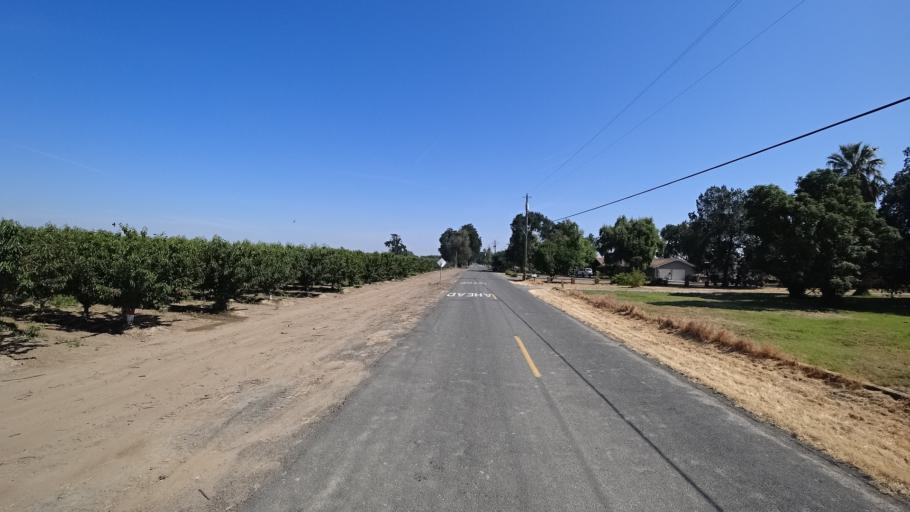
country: US
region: California
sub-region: Kings County
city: Lemoore
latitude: 36.3452
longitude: -119.8252
